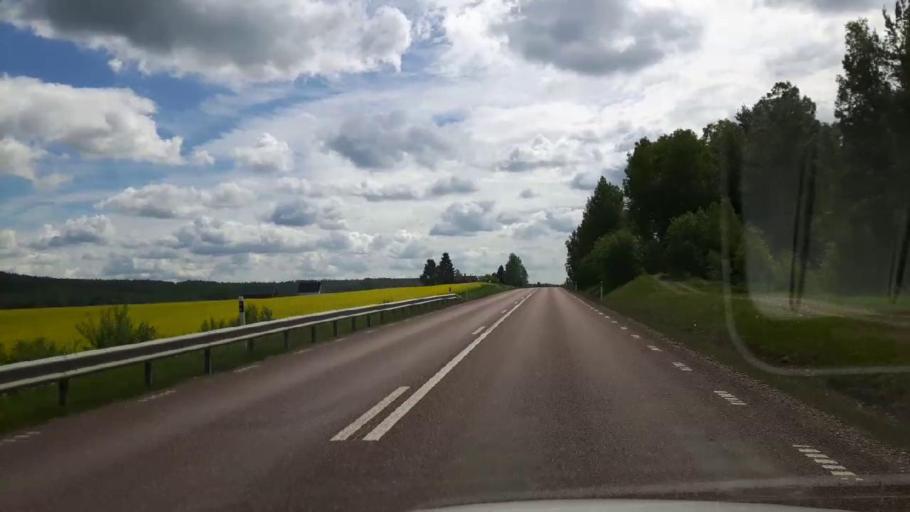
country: SE
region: Dalarna
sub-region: Hedemora Kommun
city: Hedemora
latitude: 60.3796
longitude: 15.9110
